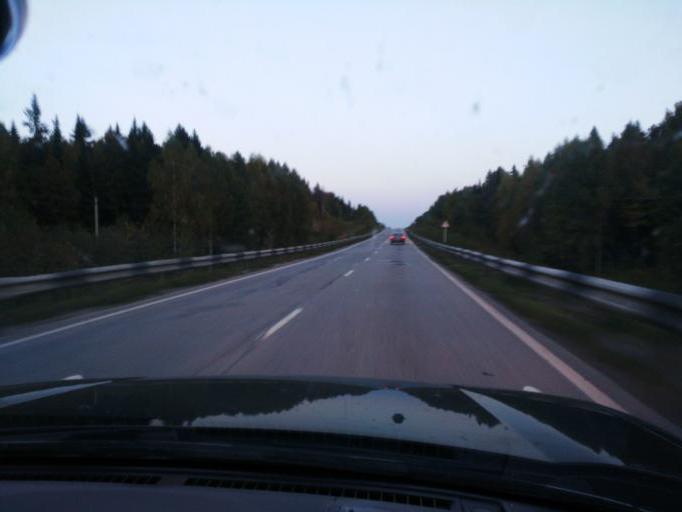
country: RU
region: Perm
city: Verkhnechusovskiye Gorodki
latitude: 58.2722
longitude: 56.9457
